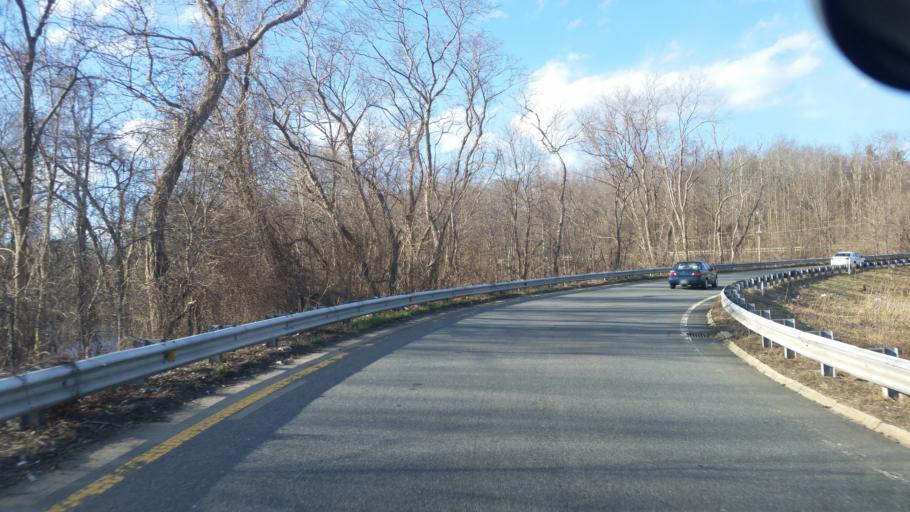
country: US
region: Massachusetts
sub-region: Essex County
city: Amesbury
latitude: 42.8471
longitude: -70.9208
